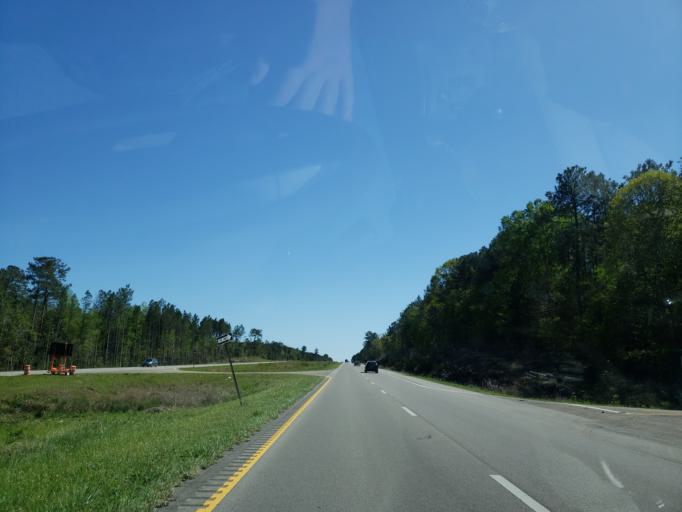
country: US
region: Mississippi
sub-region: Stone County
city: Wiggins
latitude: 31.0430
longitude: -89.2026
